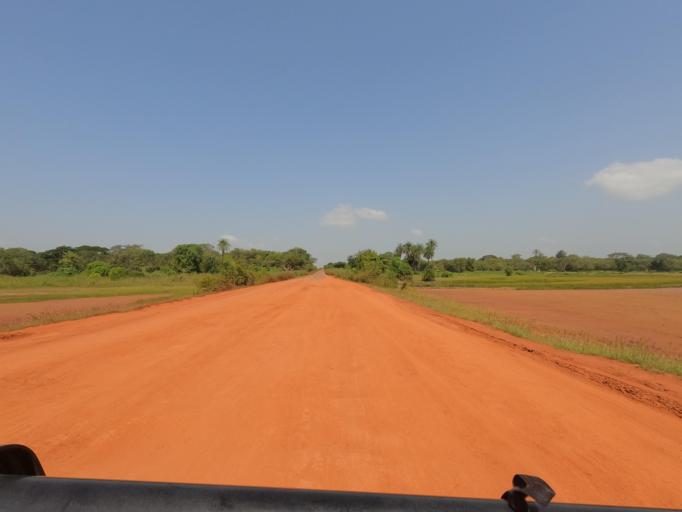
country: GW
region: Cacheu
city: Canchungo
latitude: 12.2636
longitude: -15.7848
